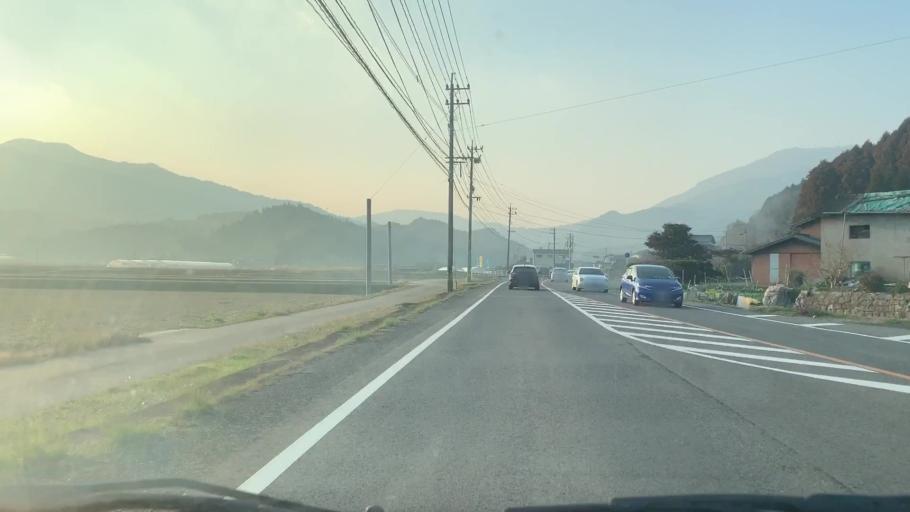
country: JP
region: Saga Prefecture
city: Takeocho-takeo
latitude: 33.2585
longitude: 130.0690
